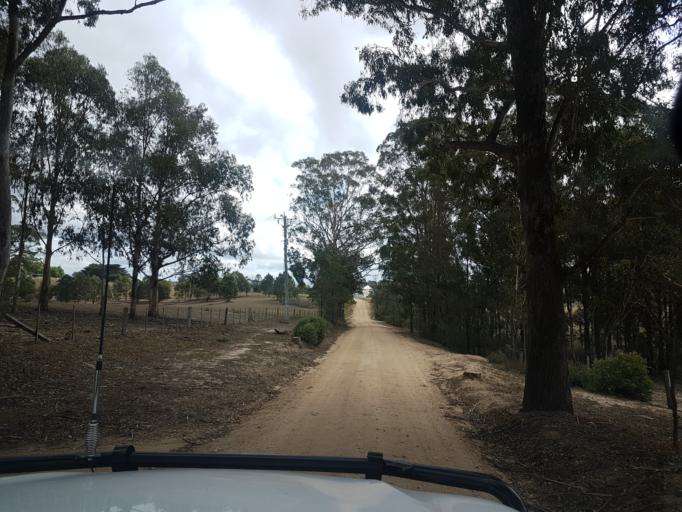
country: AU
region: Victoria
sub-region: East Gippsland
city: Bairnsdale
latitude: -37.7837
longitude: 147.5306
